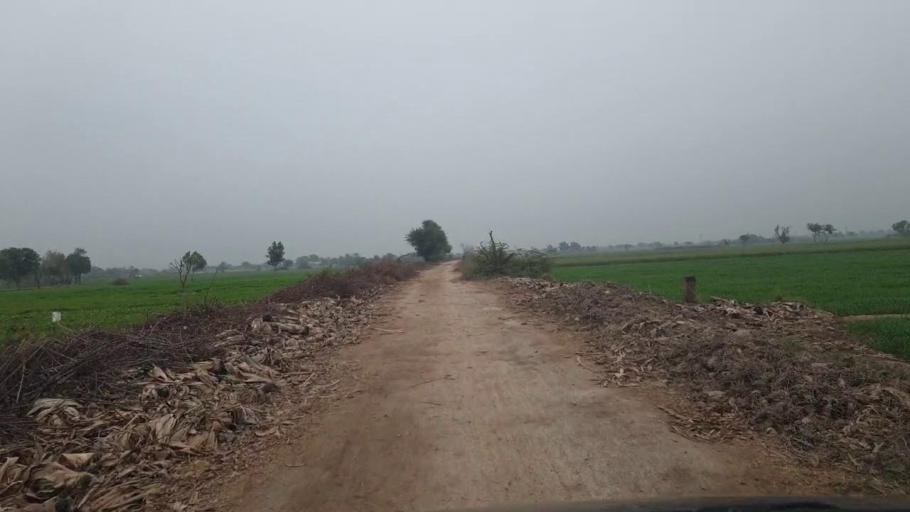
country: PK
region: Sindh
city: Tando Adam
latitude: 25.8463
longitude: 68.7036
